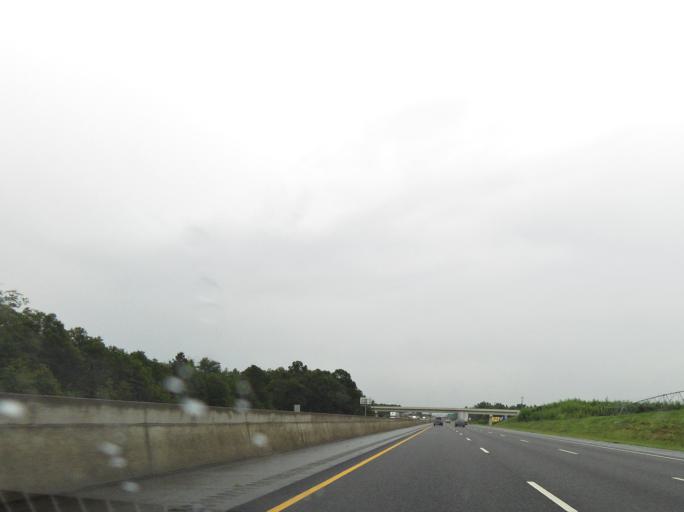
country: US
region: Georgia
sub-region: Turner County
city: Ashburn
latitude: 31.6743
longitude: -83.6148
